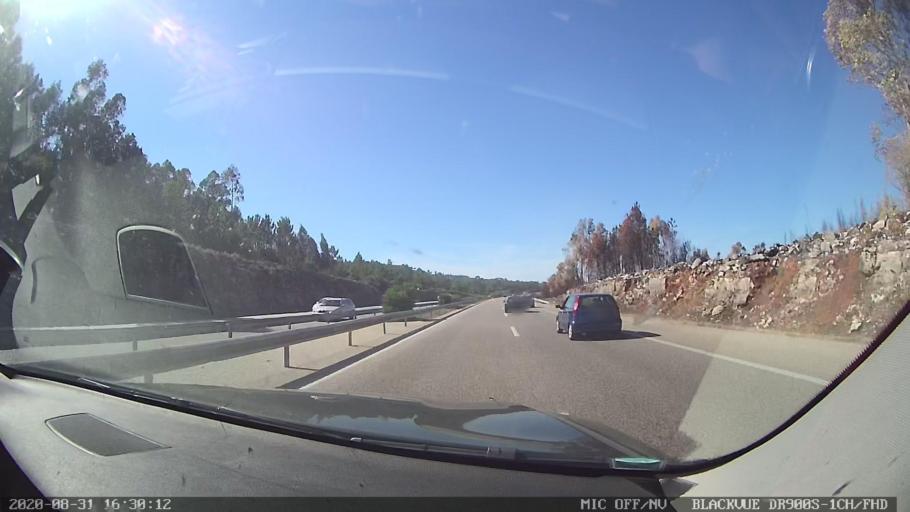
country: PT
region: Santarem
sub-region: Ourem
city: Fatima
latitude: 39.5820
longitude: -8.6580
